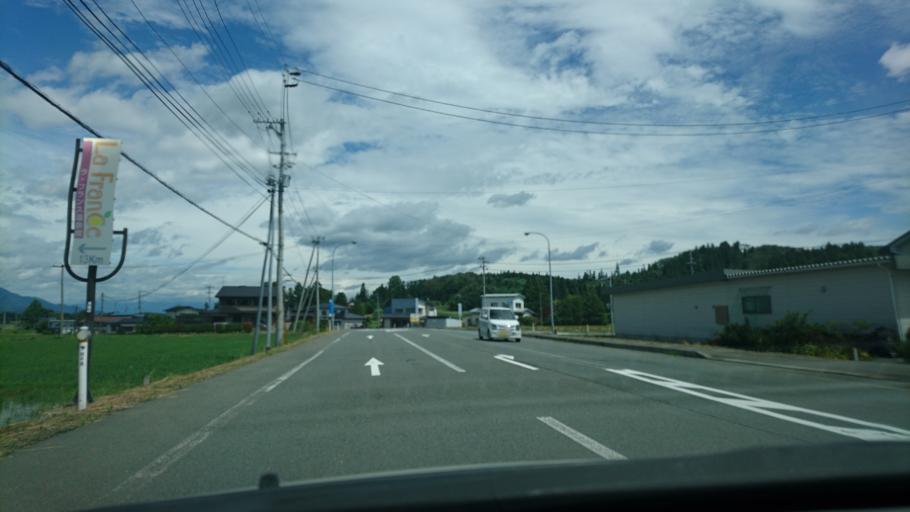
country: JP
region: Iwate
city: Hanamaki
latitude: 39.5242
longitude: 141.1939
